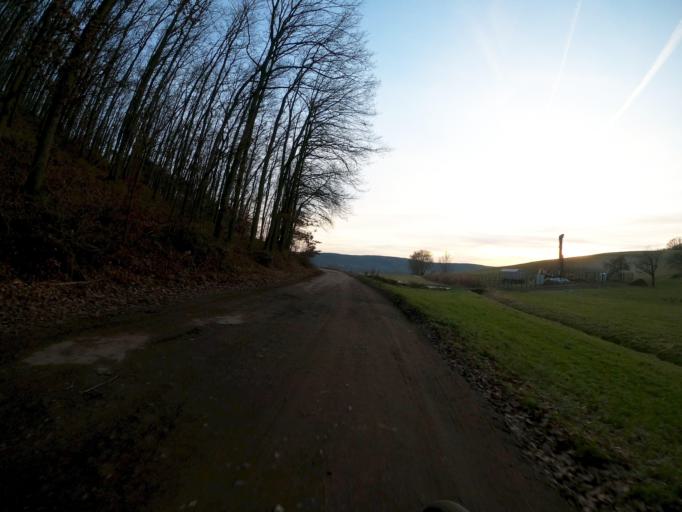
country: DE
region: Thuringia
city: Rausdorf
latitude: 50.8823
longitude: 11.6767
